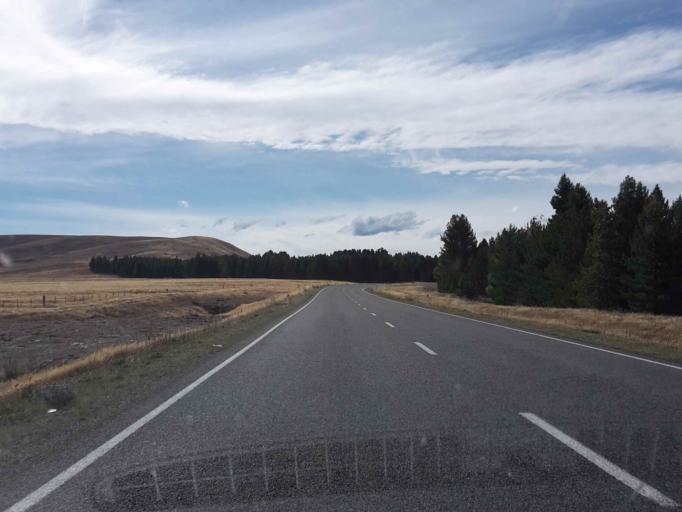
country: NZ
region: Canterbury
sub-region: Timaru District
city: Pleasant Point
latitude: -44.0171
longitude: 170.4034
